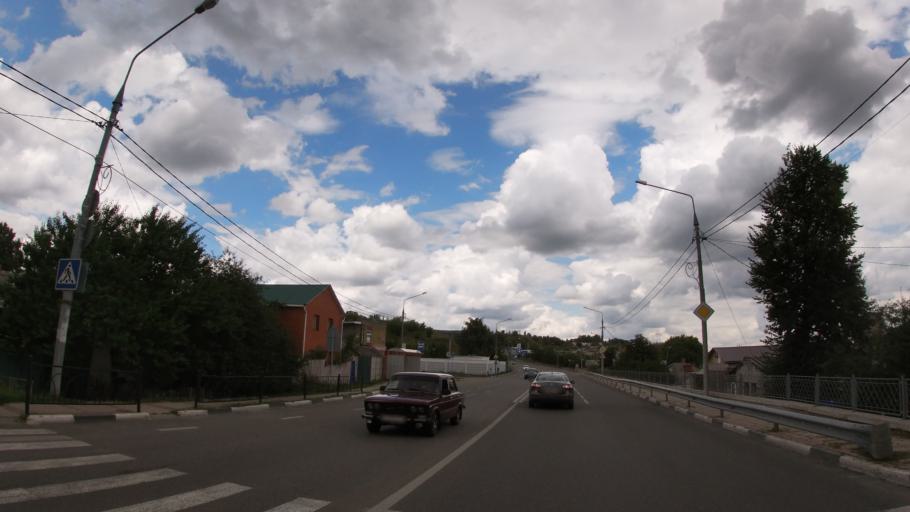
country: RU
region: Belgorod
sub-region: Belgorodskiy Rayon
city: Belgorod
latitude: 50.6075
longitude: 36.6129
